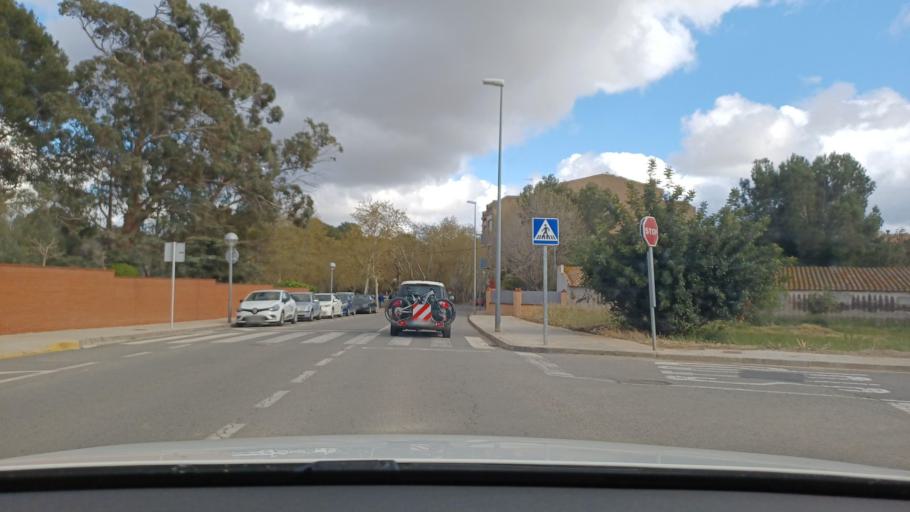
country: ES
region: Catalonia
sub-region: Provincia de Tarragona
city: Botarell
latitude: 41.1233
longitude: 1.0009
